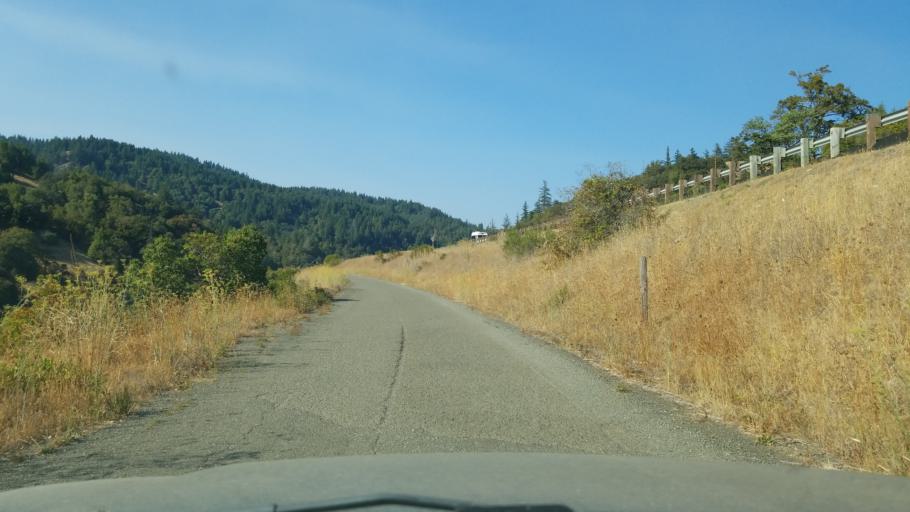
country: US
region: California
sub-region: Humboldt County
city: Redway
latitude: 40.1696
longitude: -123.7814
